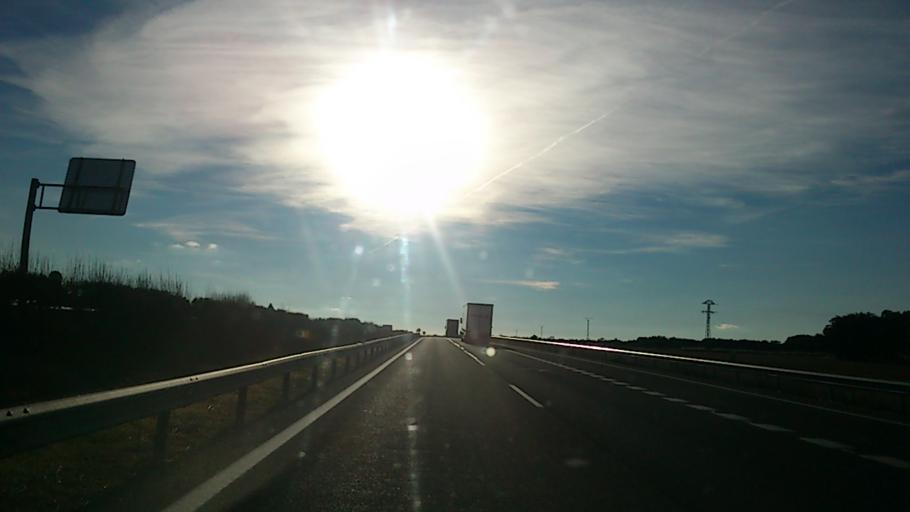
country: ES
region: Castille-La Mancha
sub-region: Provincia de Guadalajara
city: Mirabueno
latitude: 40.9269
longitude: -2.7185
